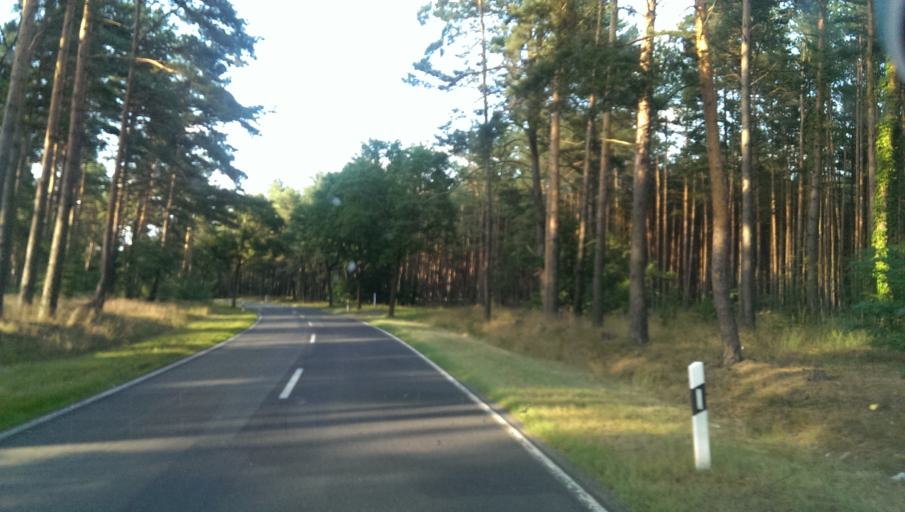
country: DE
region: Brandenburg
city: Niedergorsdorf
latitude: 52.0390
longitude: 12.9429
